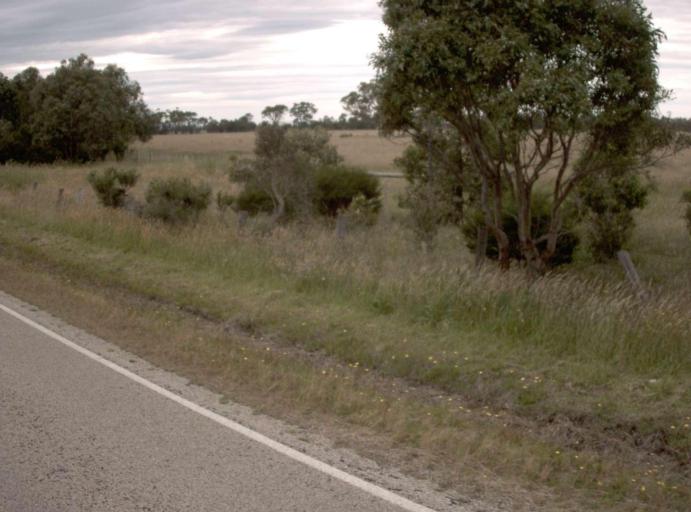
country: AU
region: Victoria
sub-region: East Gippsland
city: Bairnsdale
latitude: -37.9031
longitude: 147.5521
